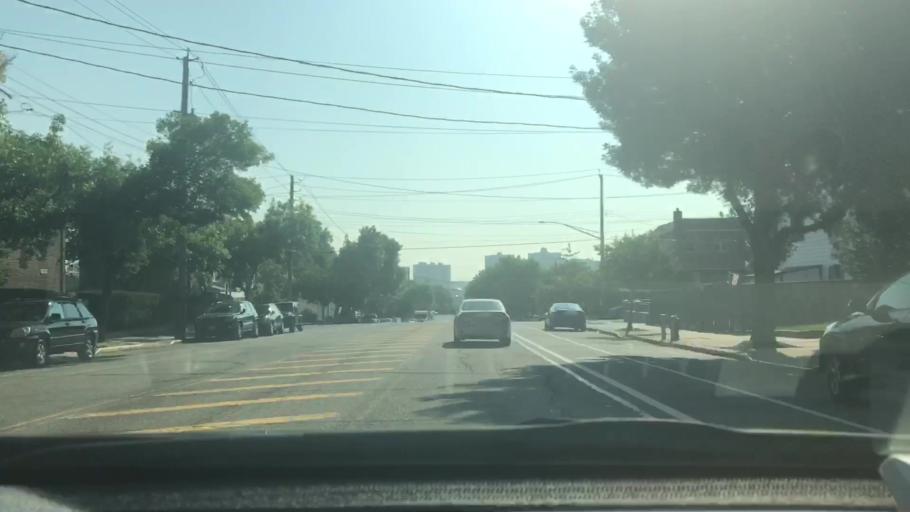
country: US
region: New York
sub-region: Bronx
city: Eastchester
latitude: 40.8652
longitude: -73.8443
